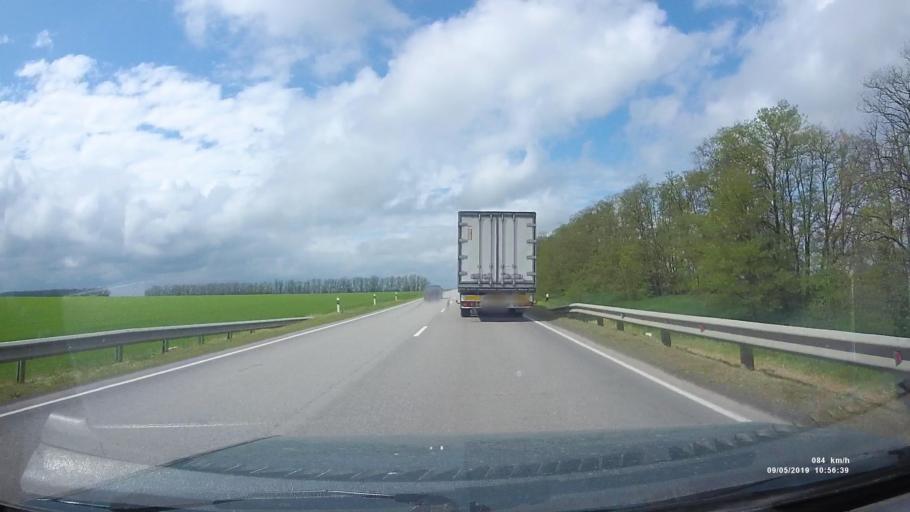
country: RU
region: Rostov
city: Peshkovo
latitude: 46.8684
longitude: 39.2950
